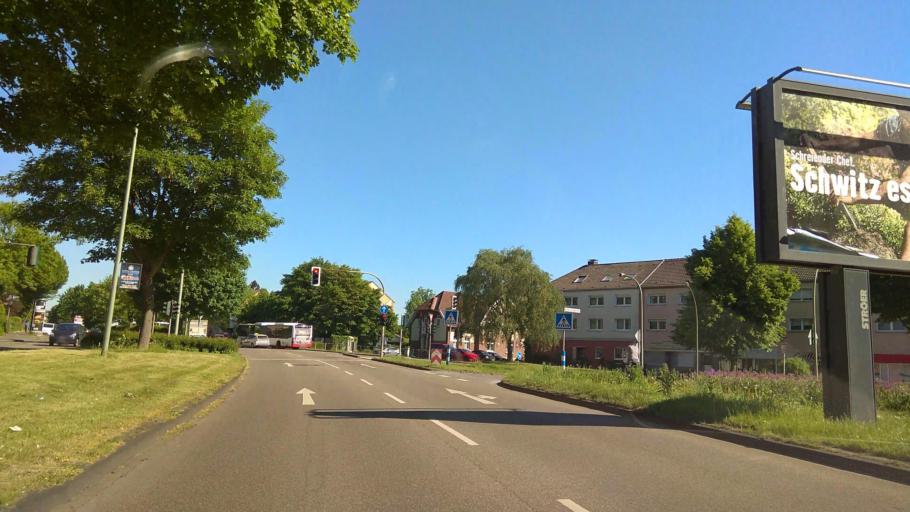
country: DE
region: North Rhine-Westphalia
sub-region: Regierungsbezirk Munster
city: Bottrop
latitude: 51.5148
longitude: 6.9346
